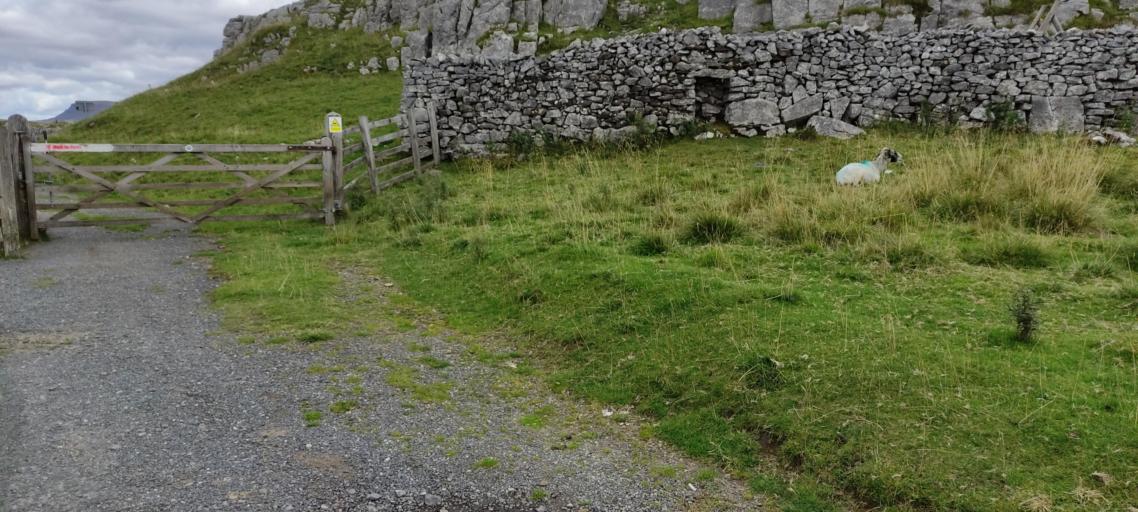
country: GB
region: England
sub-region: North Yorkshire
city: Settle
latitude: 54.0887
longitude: -2.2549
